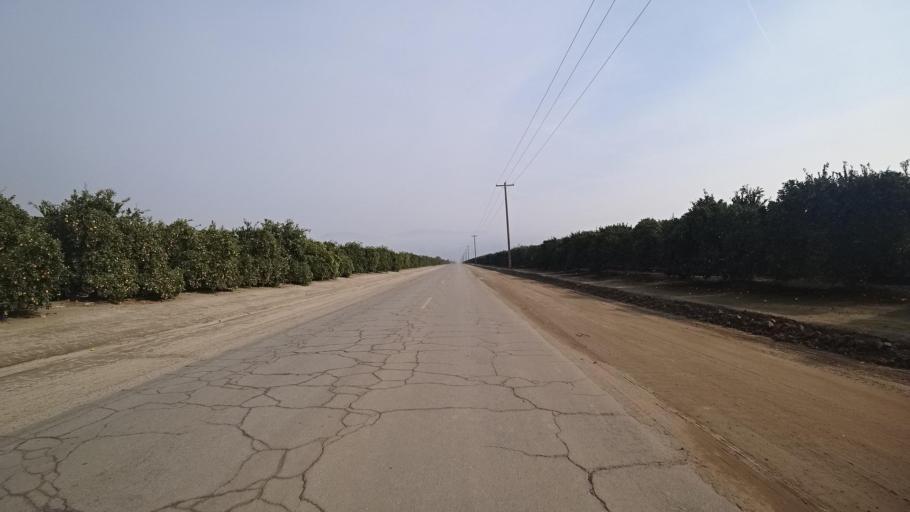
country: US
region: California
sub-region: Kern County
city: Arvin
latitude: 35.1509
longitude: -118.8593
